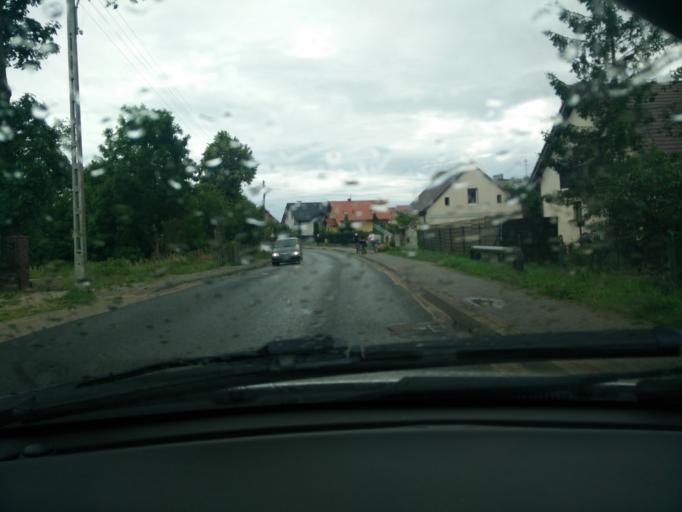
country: PL
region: Pomeranian Voivodeship
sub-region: Powiat pucki
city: Mosty
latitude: 54.6119
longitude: 18.4961
